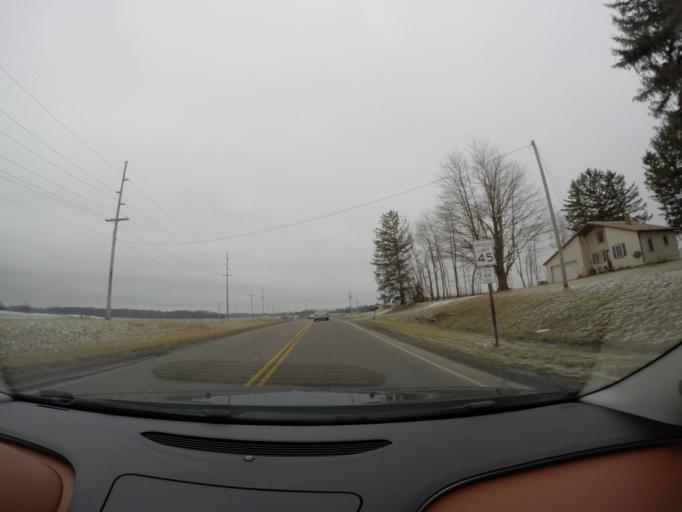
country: US
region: Ohio
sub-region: Wayne County
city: Smithville
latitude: 40.8142
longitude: -81.8444
